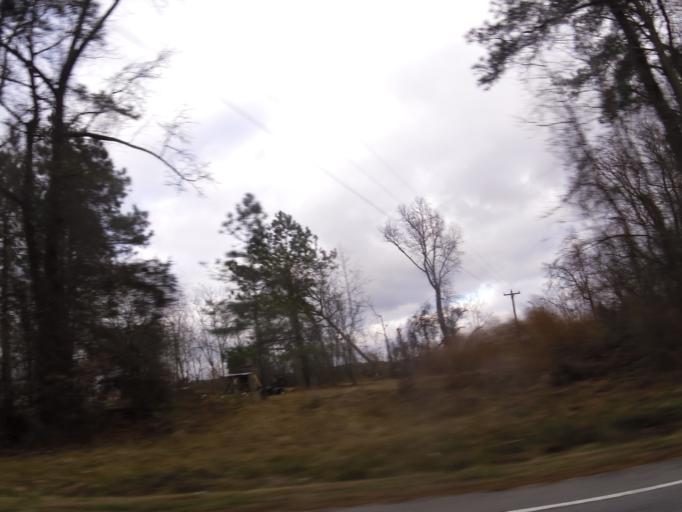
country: US
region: North Carolina
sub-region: Edgecombe County
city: Pinetops
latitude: 35.8569
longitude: -77.6886
